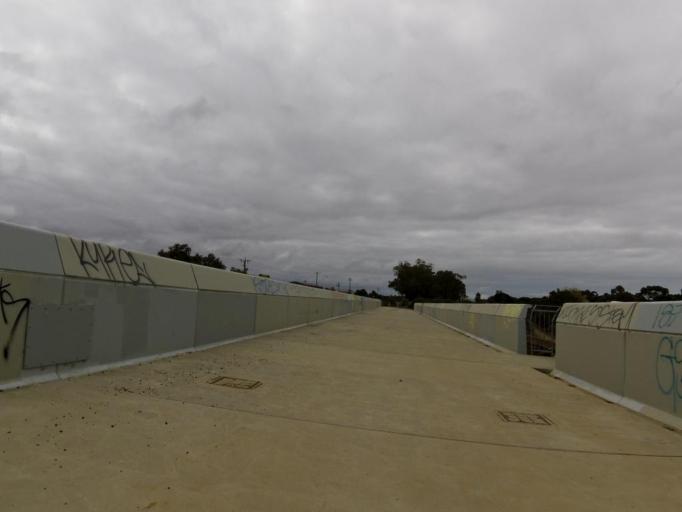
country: AU
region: Victoria
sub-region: Wyndham
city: Werribee
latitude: -37.9197
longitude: 144.6568
